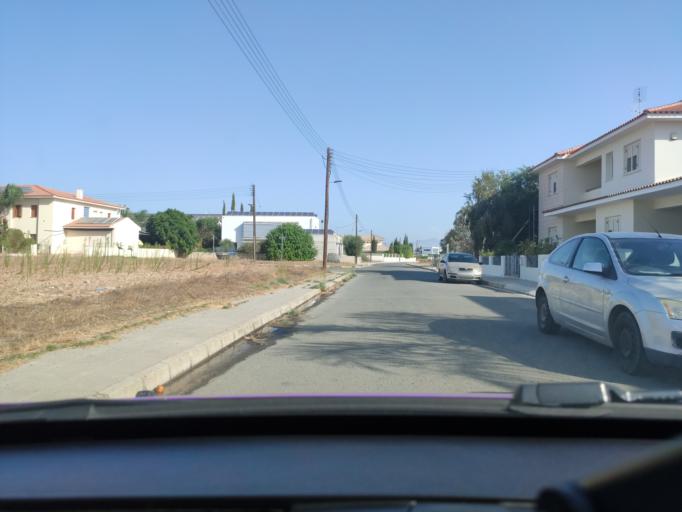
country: CY
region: Lefkosia
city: Tseri
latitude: 35.1060
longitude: 33.3520
